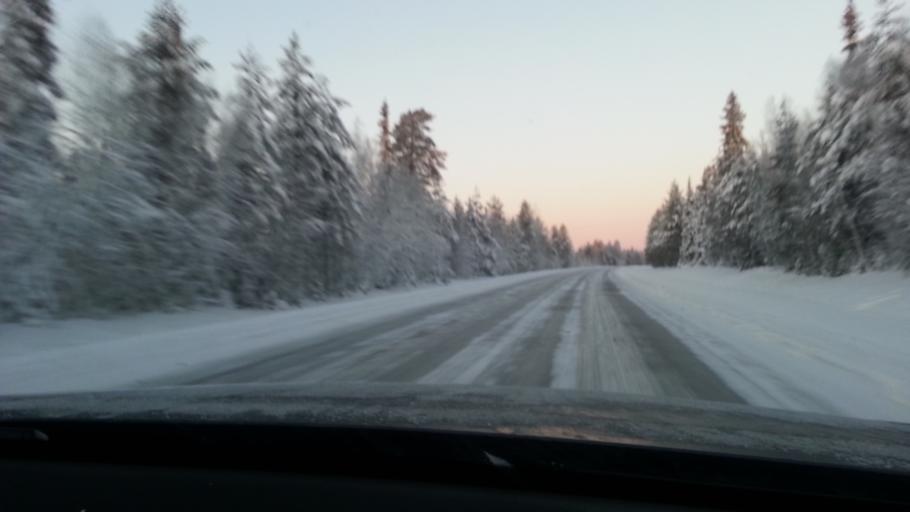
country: FI
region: Lapland
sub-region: Tunturi-Lappi
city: Kittilae
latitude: 67.2154
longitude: 24.9256
